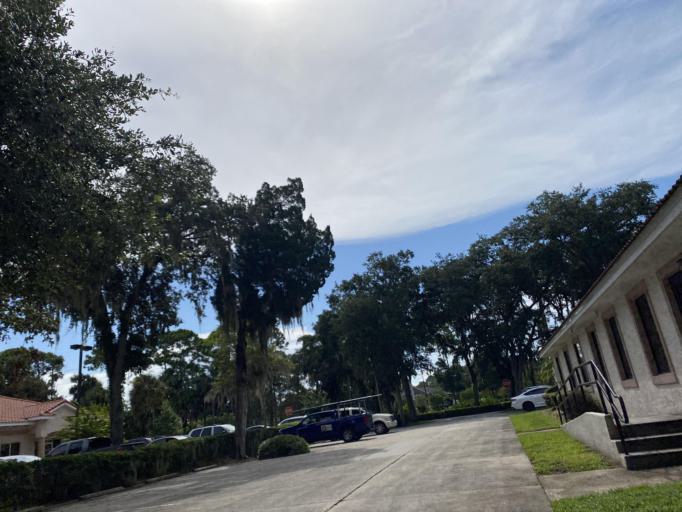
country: US
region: Florida
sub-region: Volusia County
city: Port Orange
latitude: 29.1360
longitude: -81.0002
